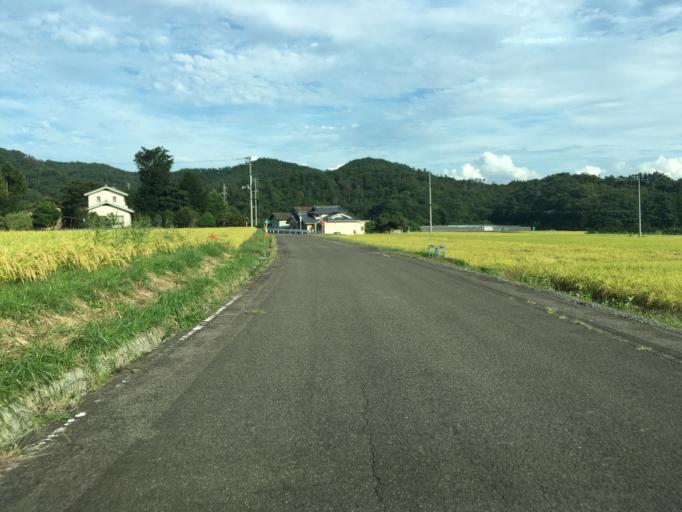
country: JP
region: Fukushima
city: Hobaramachi
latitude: 37.8890
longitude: 140.5301
